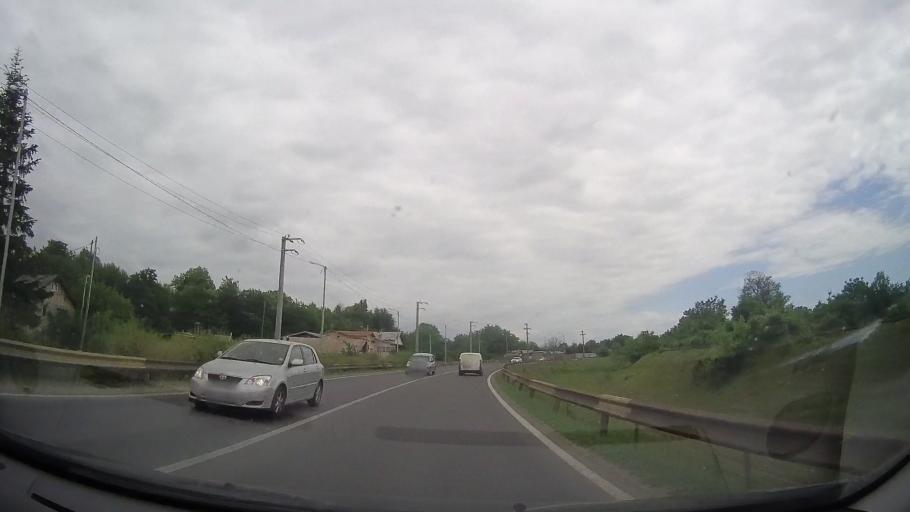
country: RO
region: Prahova
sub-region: Comuna Blejoiu
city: Blejoi
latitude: 44.9927
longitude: 26.0129
